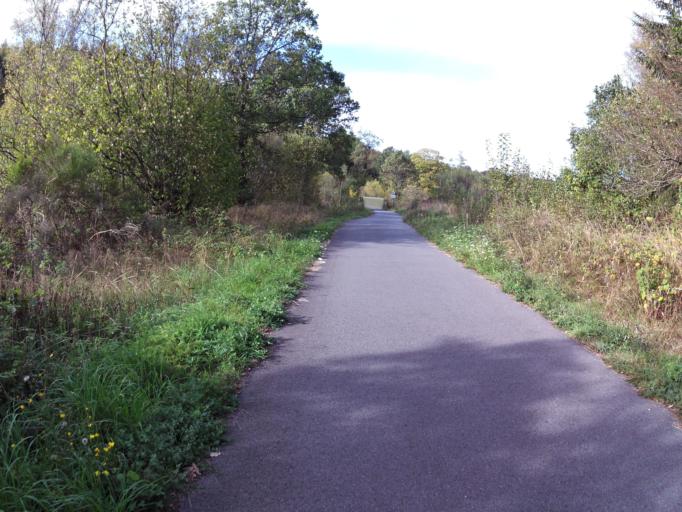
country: BE
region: Wallonia
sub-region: Province de Liege
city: Saint-Vith
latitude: 50.2434
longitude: 6.1540
